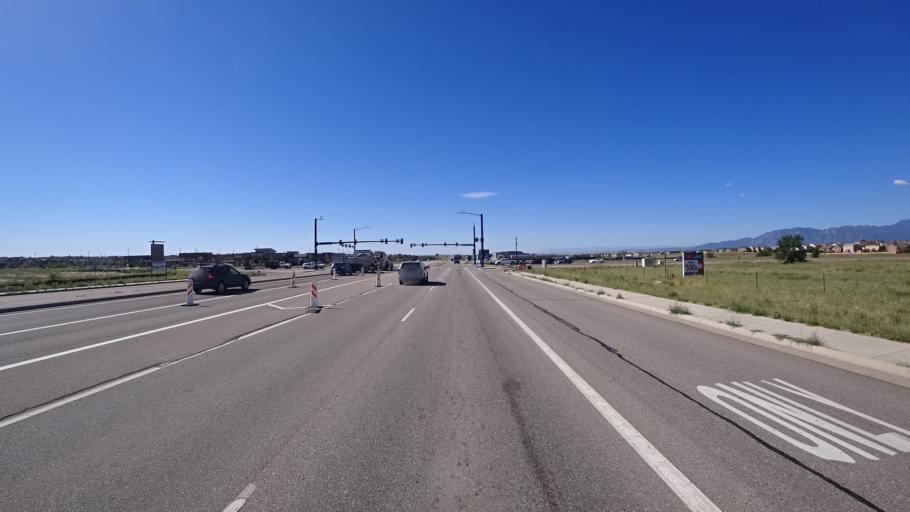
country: US
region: Colorado
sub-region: El Paso County
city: Cimarron Hills
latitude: 38.8689
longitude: -104.6829
